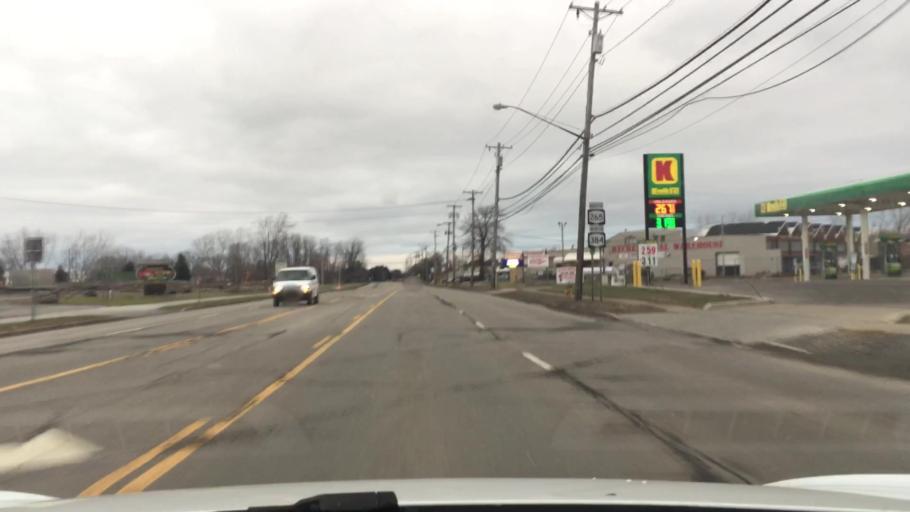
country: US
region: New York
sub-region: Erie County
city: Tonawanda
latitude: 43.0353
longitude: -78.8844
